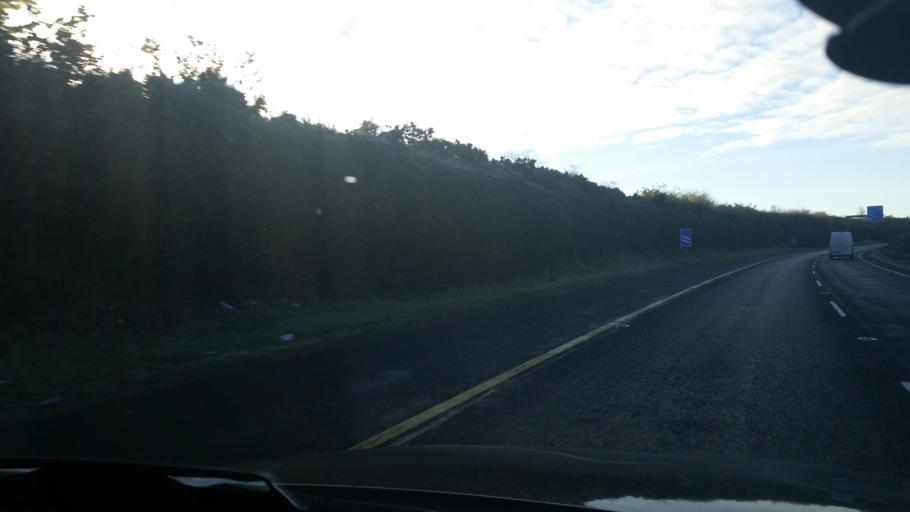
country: IE
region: Leinster
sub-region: Wicklow
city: Arklow
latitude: 52.7804
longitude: -6.1759
